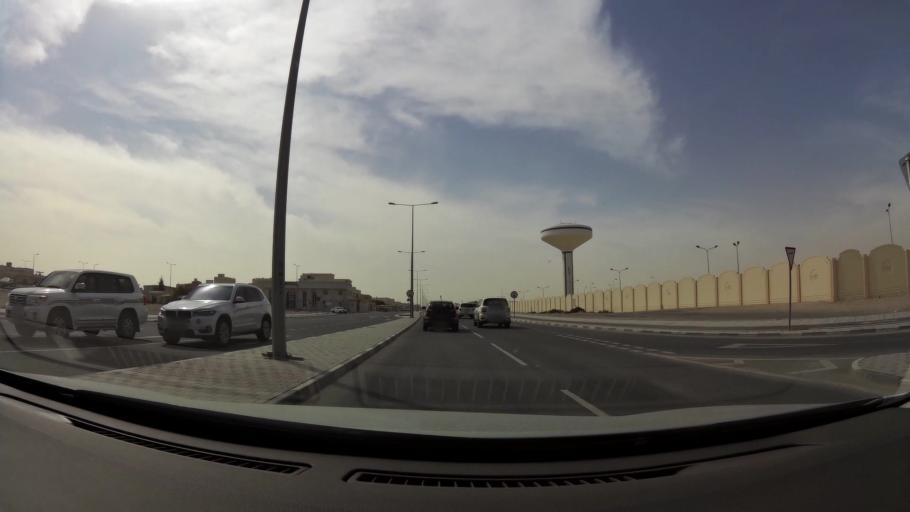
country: QA
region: Baladiyat ar Rayyan
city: Ar Rayyan
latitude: 25.3195
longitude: 51.4055
